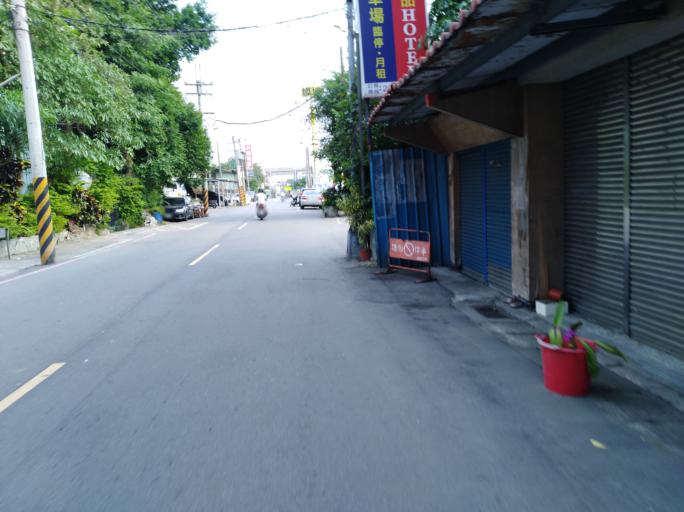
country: TW
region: Taipei
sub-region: Taipei
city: Banqiao
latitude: 25.0381
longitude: 121.4247
